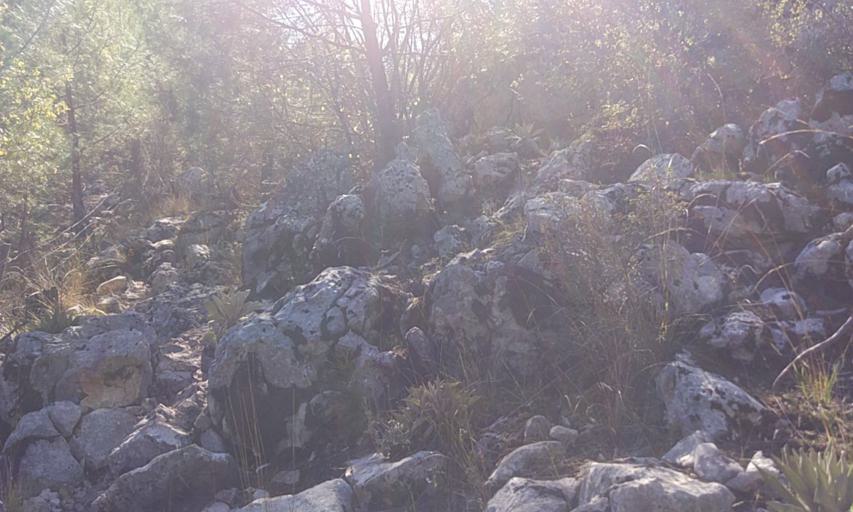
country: TR
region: Antalya
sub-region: Kemer
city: Goeynuek
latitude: 36.6343
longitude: 30.4470
